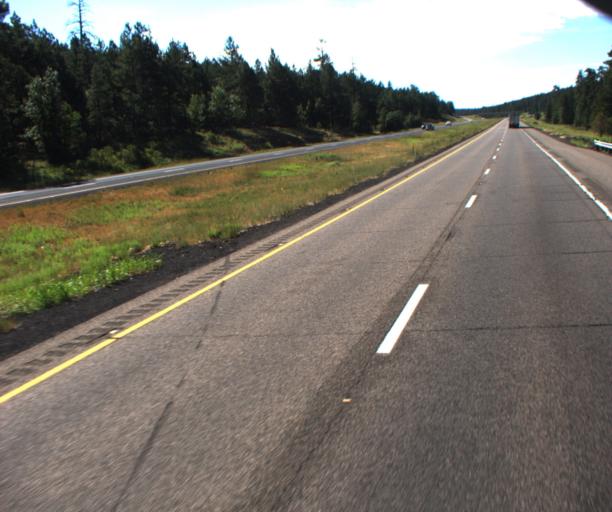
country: US
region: Arizona
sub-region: Coconino County
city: Sedona
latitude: 34.8831
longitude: -111.6401
